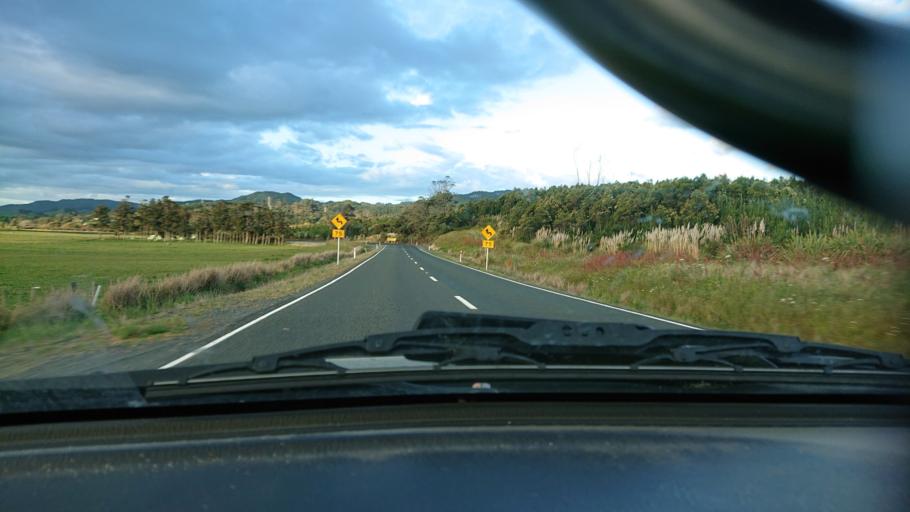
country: NZ
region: Auckland
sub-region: Auckland
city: Parakai
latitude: -36.5153
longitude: 174.4515
